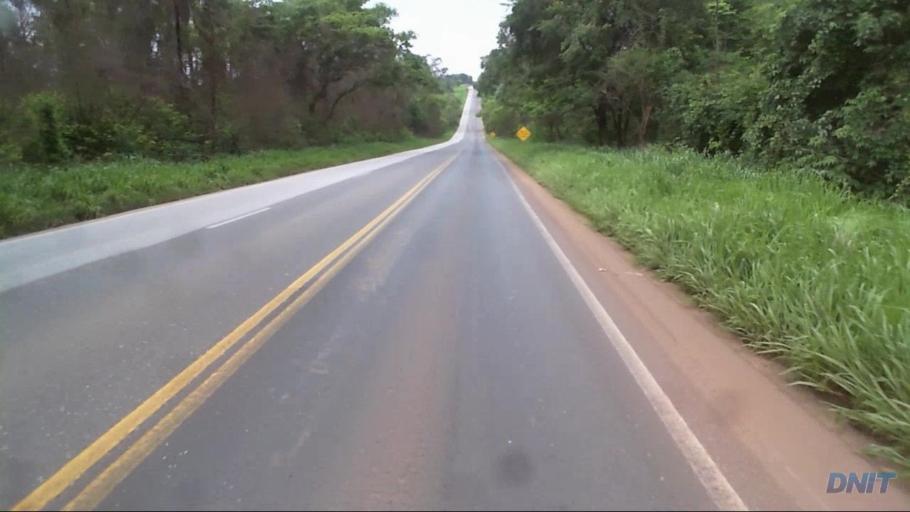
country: BR
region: Goias
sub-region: Uruacu
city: Uruacu
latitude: -14.5883
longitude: -49.1617
